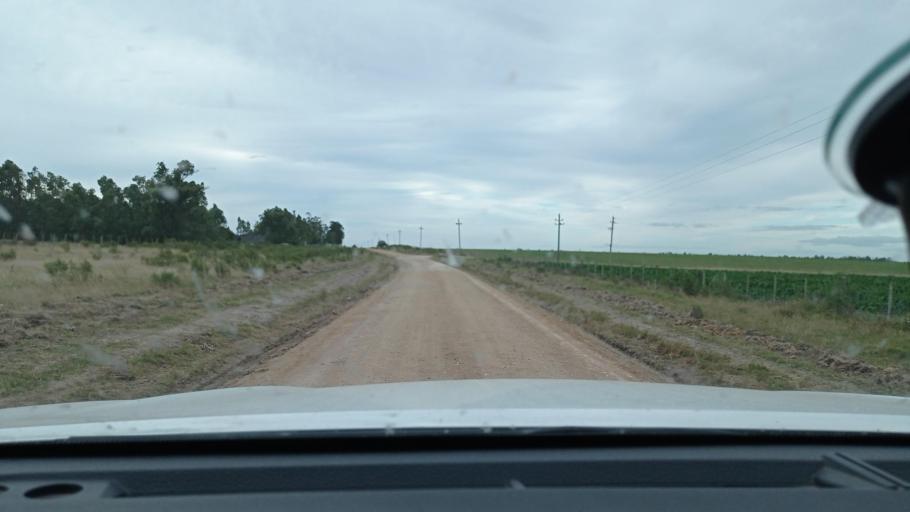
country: UY
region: Florida
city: Casupa
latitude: -34.1105
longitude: -55.7653
